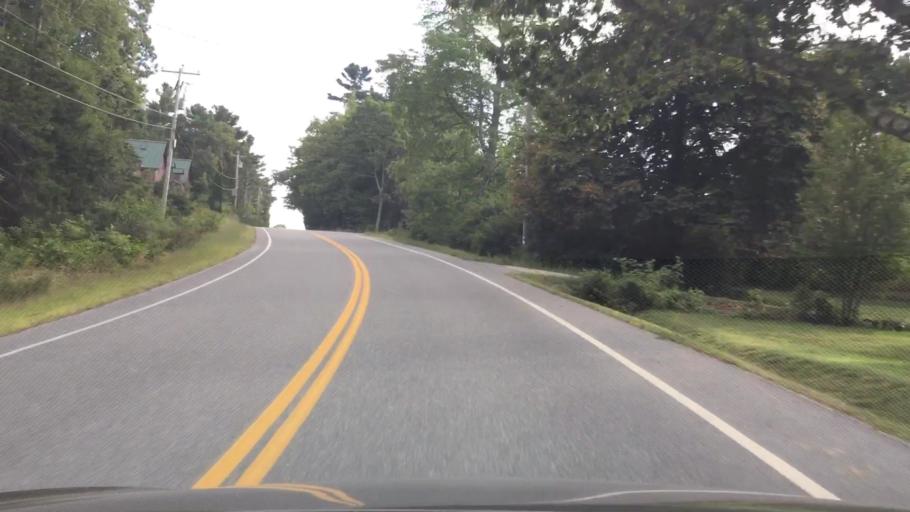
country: US
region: Maine
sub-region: Hancock County
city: Castine
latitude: 44.4460
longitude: -68.7861
